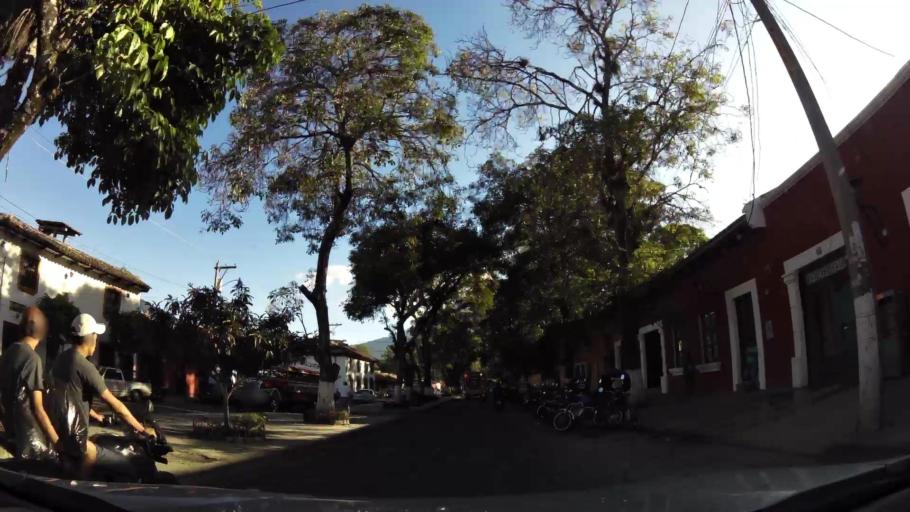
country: GT
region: Sacatepequez
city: Antigua Guatemala
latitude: 14.5557
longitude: -90.7380
